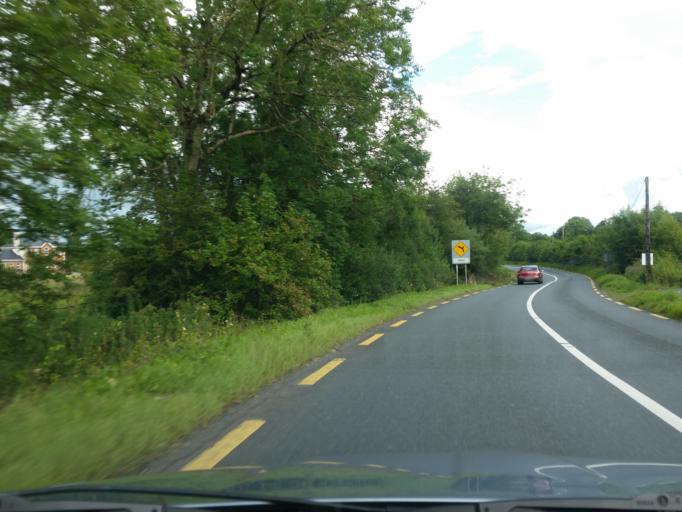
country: IE
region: Ulster
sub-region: An Cabhan
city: Belturbet
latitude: 54.1144
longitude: -7.3523
